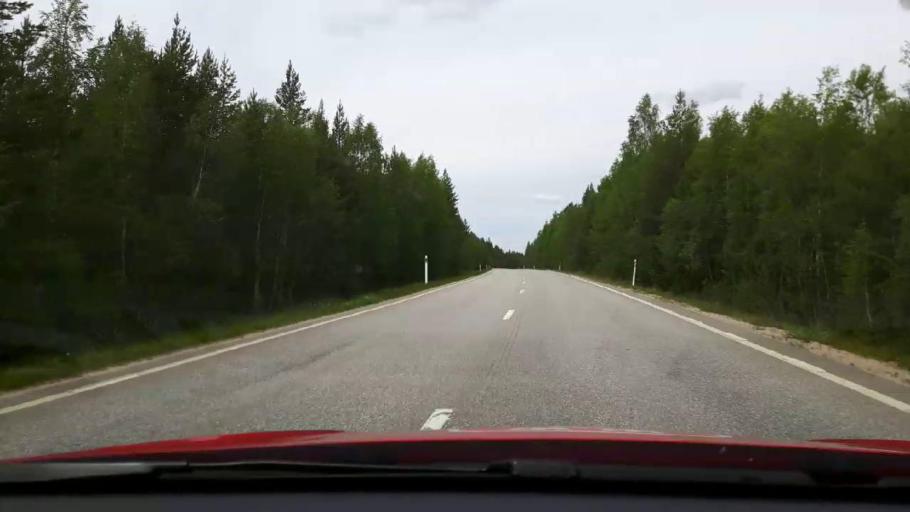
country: SE
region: Jaemtland
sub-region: Harjedalens Kommun
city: Sveg
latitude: 62.0778
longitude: 14.2643
